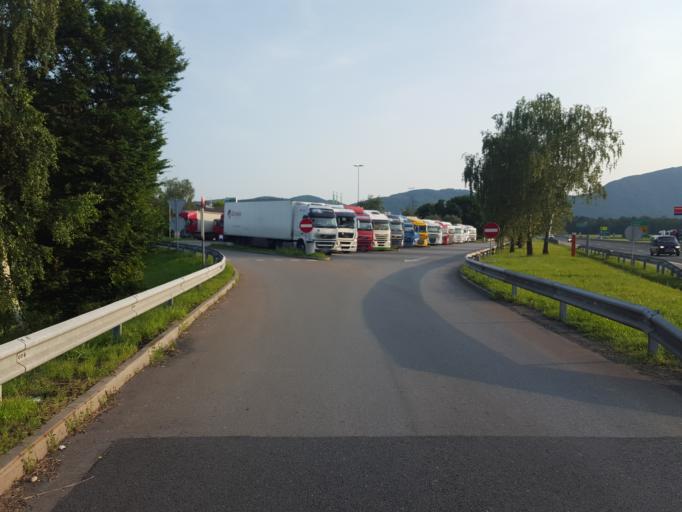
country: SI
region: Oplotnica
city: Oplotnica
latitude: 46.3491
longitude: 15.4890
